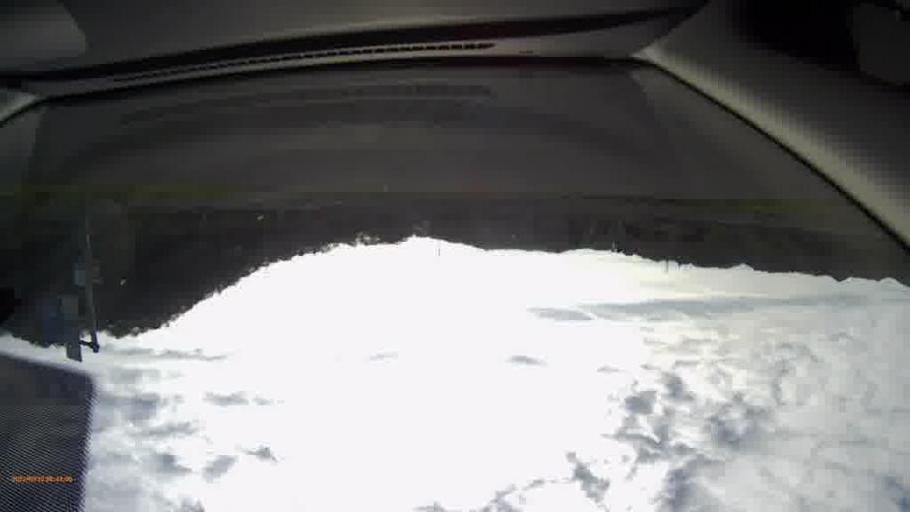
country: JP
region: Hokkaido
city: Kushiro
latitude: 43.0771
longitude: 143.9632
